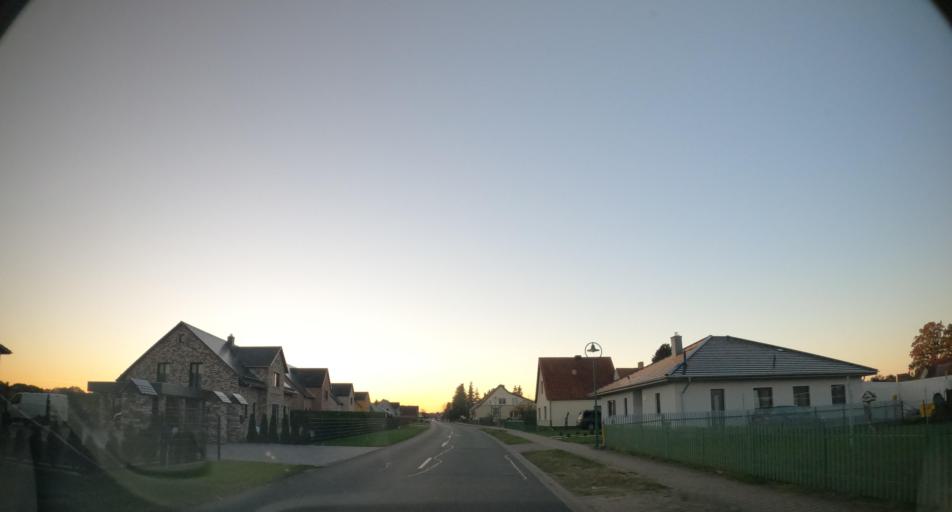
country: DE
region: Mecklenburg-Vorpommern
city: Ueckermunde
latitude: 53.7670
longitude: 13.9736
